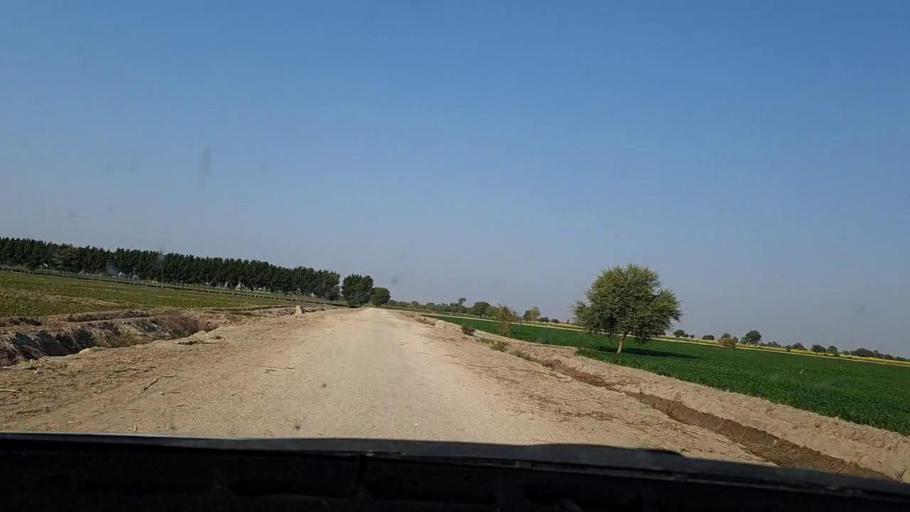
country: PK
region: Sindh
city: Tando Mittha Khan
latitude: 25.8264
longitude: 69.3064
